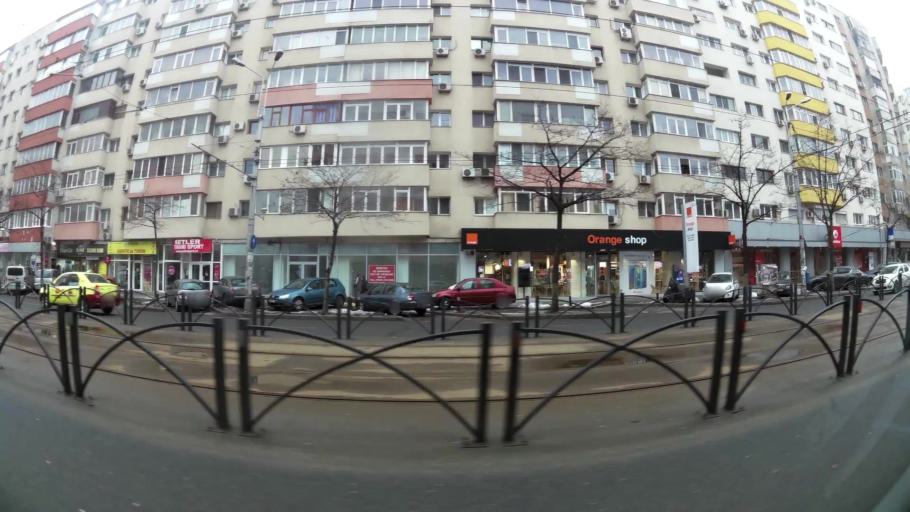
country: RO
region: Bucuresti
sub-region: Municipiul Bucuresti
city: Bucharest
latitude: 44.4452
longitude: 26.1208
